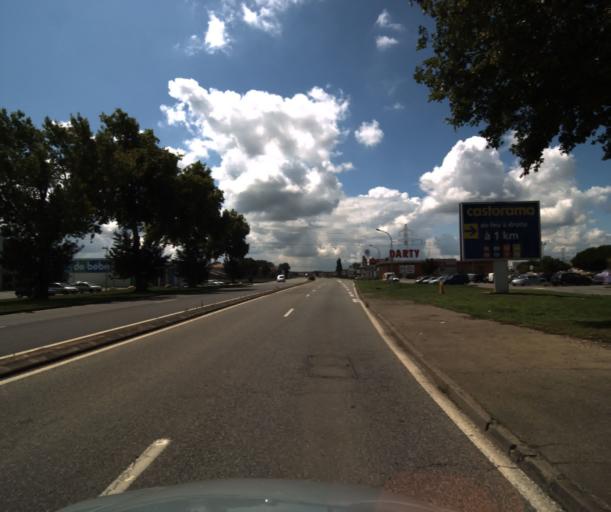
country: FR
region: Midi-Pyrenees
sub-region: Departement de la Haute-Garonne
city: Portet-sur-Garonne
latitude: 43.5329
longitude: 1.4077
